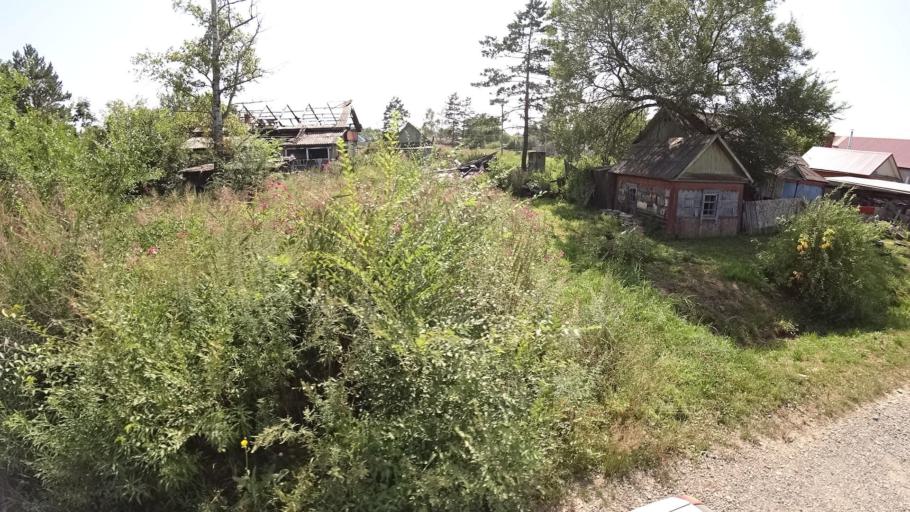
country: RU
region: Khabarovsk Krai
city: Khor
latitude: 47.9699
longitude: 135.0575
